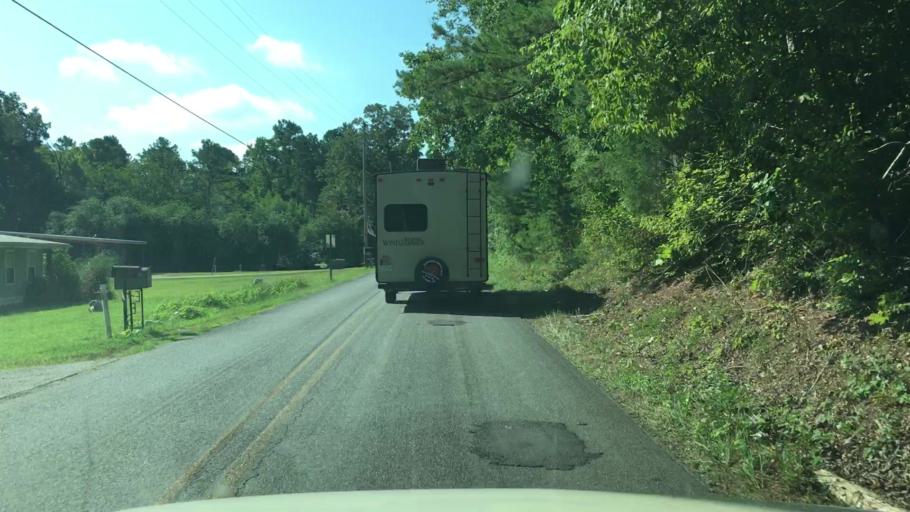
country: US
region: Arkansas
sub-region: Garland County
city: Piney
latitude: 34.5294
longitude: -93.3363
